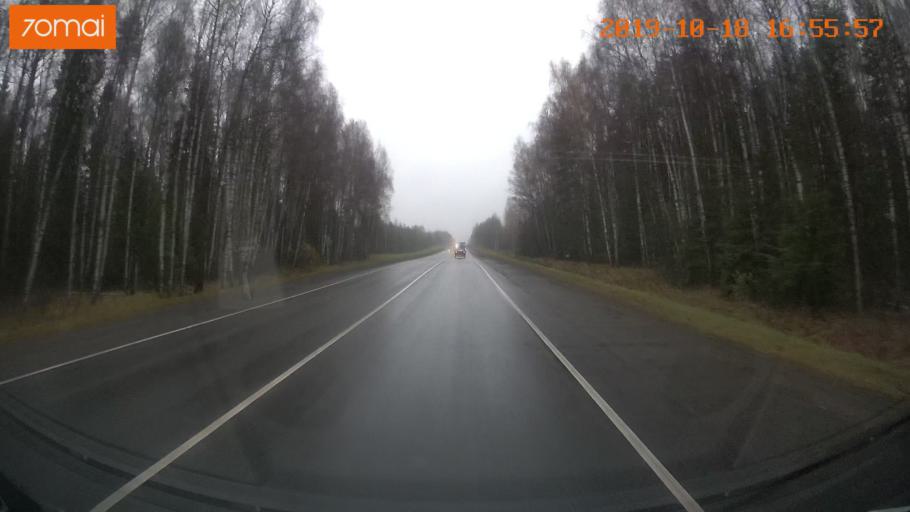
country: RU
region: Ivanovo
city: Novoye Leushino
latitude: 56.6511
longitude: 40.5842
